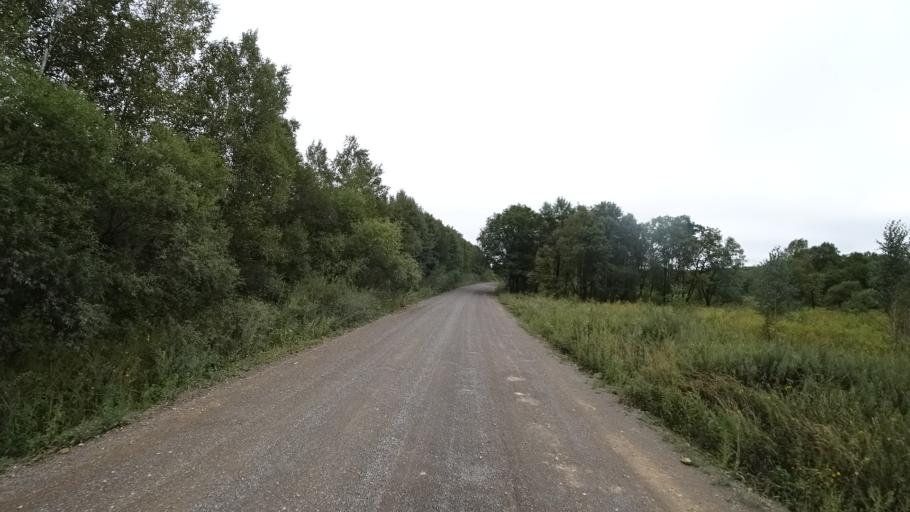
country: RU
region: Primorskiy
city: Ivanovka
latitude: 44.0446
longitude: 132.4930
